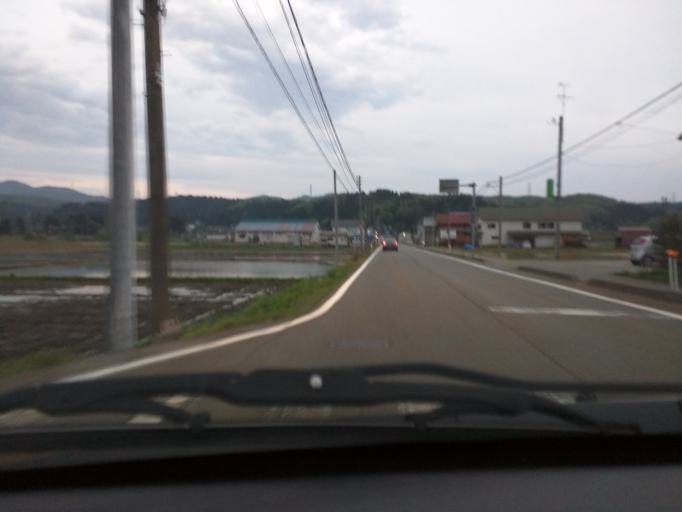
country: JP
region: Niigata
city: Ojiya
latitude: 37.3205
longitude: 138.7179
